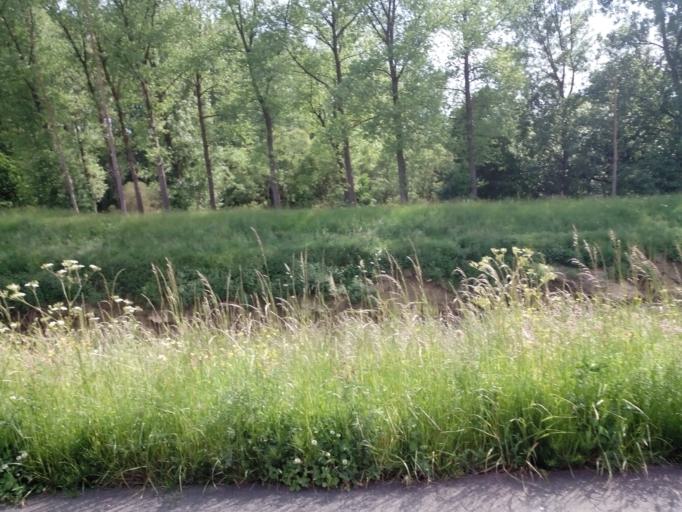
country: BE
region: Flanders
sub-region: Provincie Vlaams-Brabant
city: Rotselaar
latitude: 50.9704
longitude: 4.7237
